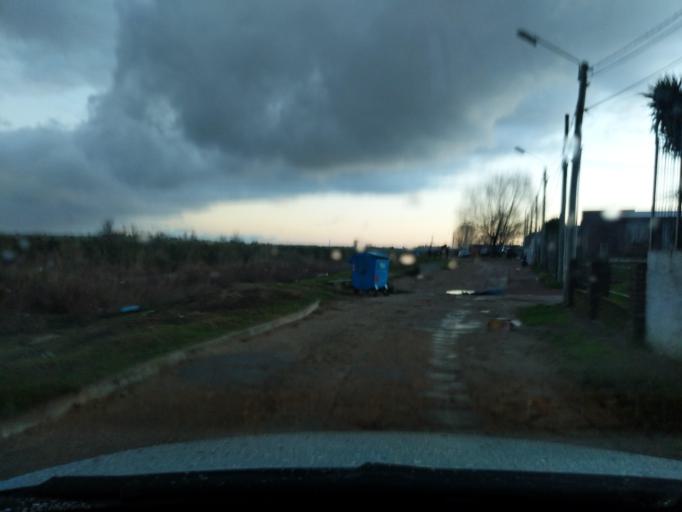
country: UY
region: Florida
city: Florida
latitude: -34.1094
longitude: -56.2071
